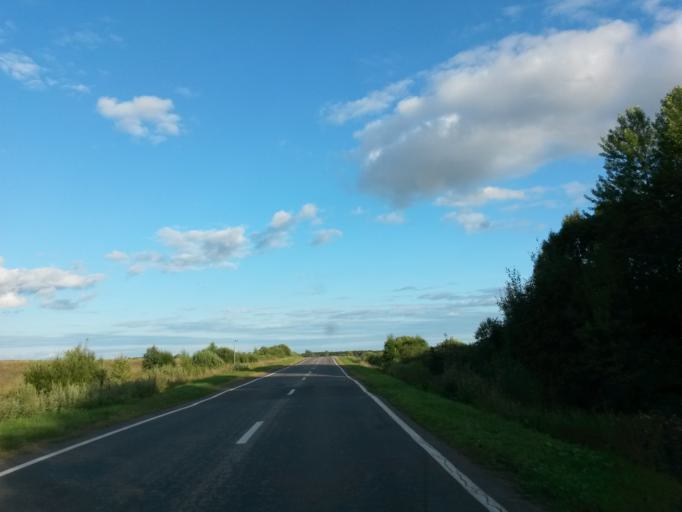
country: RU
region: Jaroslavl
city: Konstantinovskiy
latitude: 57.8386
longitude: 39.6553
